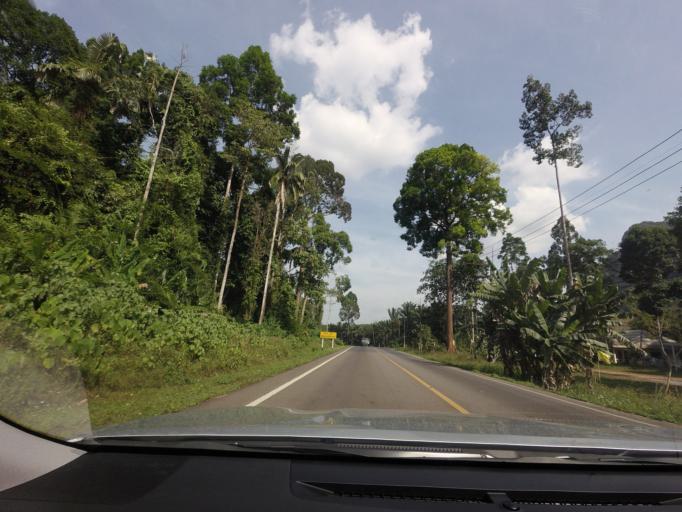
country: TH
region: Krabi
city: Krabi
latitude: 8.1414
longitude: 98.8532
